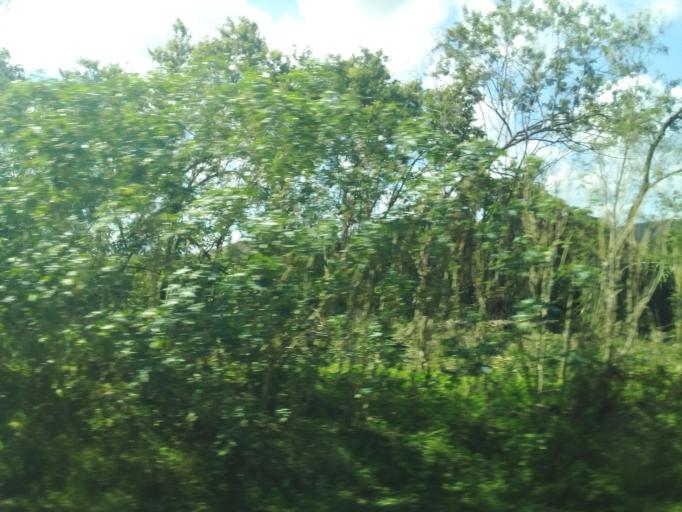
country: BR
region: Minas Gerais
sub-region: Governador Valadares
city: Governador Valadares
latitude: -18.8690
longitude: -41.7754
